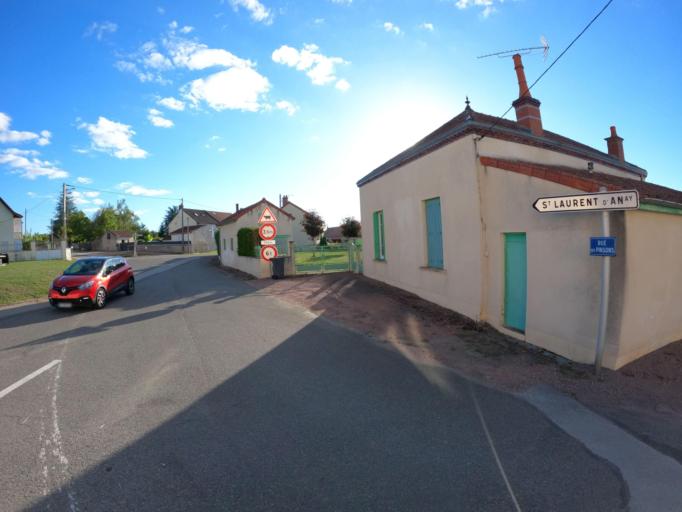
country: FR
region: Bourgogne
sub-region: Departement de Saone-et-Loire
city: Ecuisses
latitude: 46.7519
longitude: 4.5233
